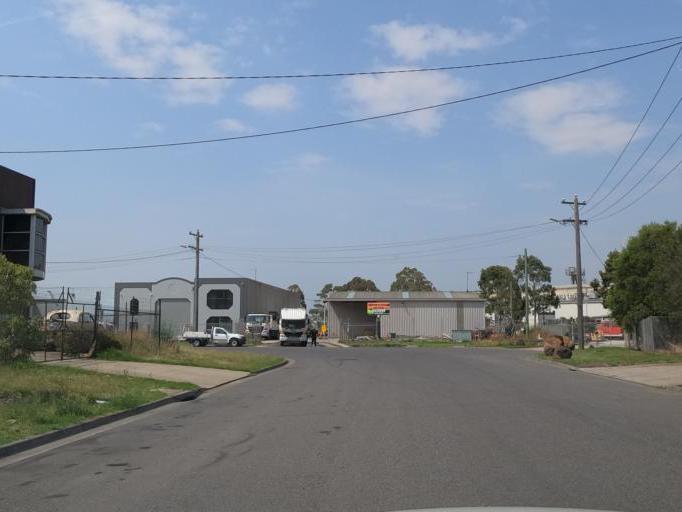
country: AU
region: Victoria
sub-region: Hume
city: Coolaroo
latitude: -37.6472
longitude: 144.9387
